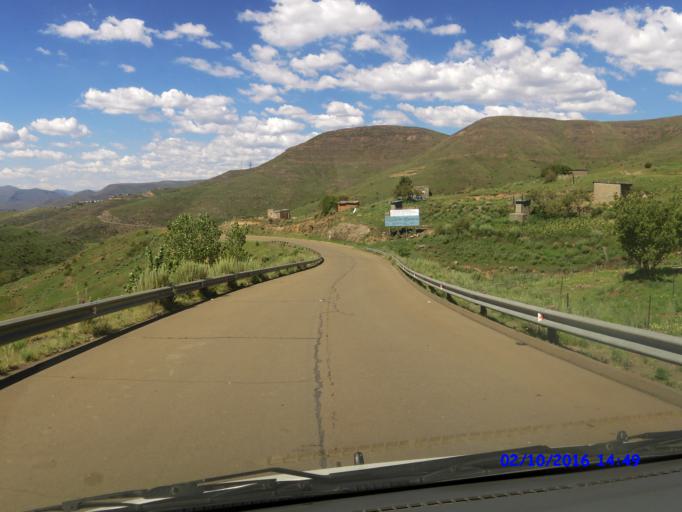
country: LS
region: Maseru
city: Nako
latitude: -29.4927
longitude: 28.0600
